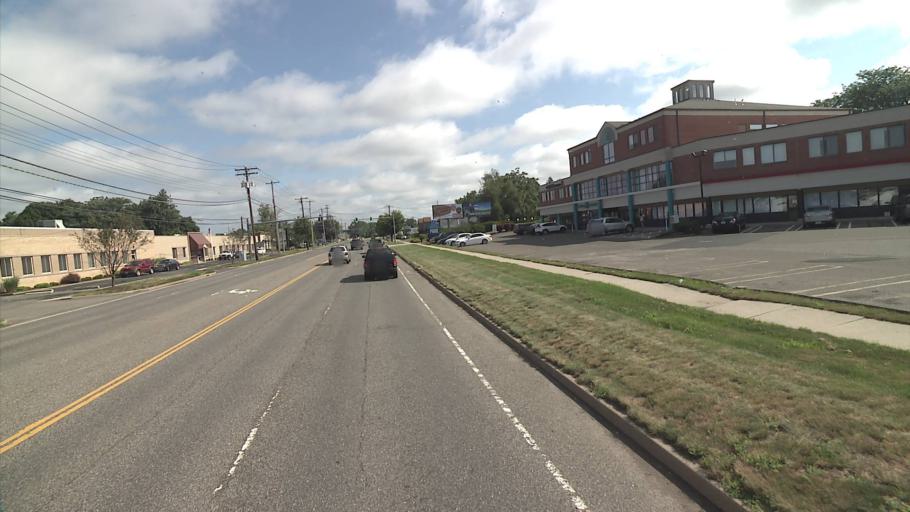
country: US
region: Connecticut
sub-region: New Haven County
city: City of Milford (balance)
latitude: 41.2238
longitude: -73.0721
